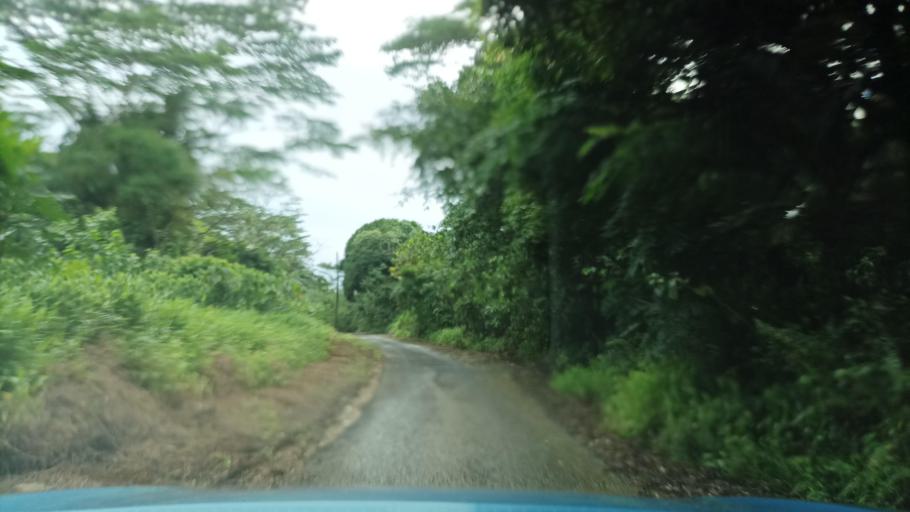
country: FM
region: Pohnpei
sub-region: Sokehs Municipality
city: Palikir - National Government Center
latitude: 6.8800
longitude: 158.1660
